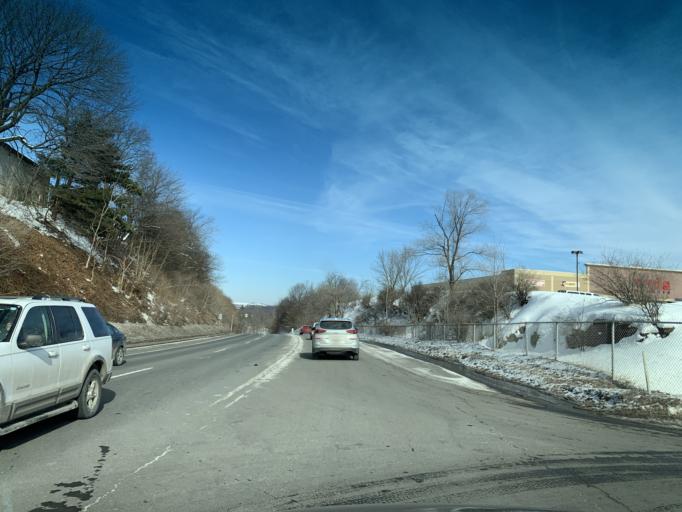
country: US
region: Maryland
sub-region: Allegany County
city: Frostburg
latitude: 39.6515
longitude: -78.9105
